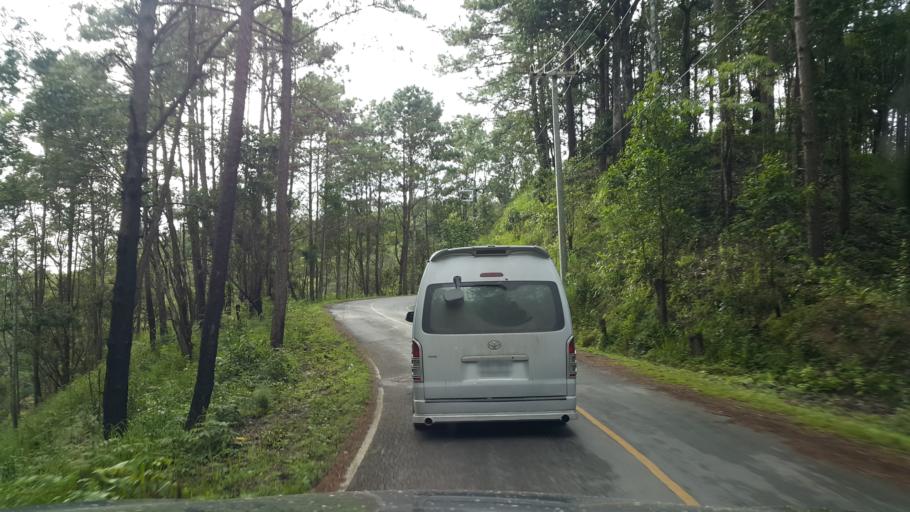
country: TH
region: Chiang Mai
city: Chaem Luang
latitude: 18.9326
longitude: 98.4769
